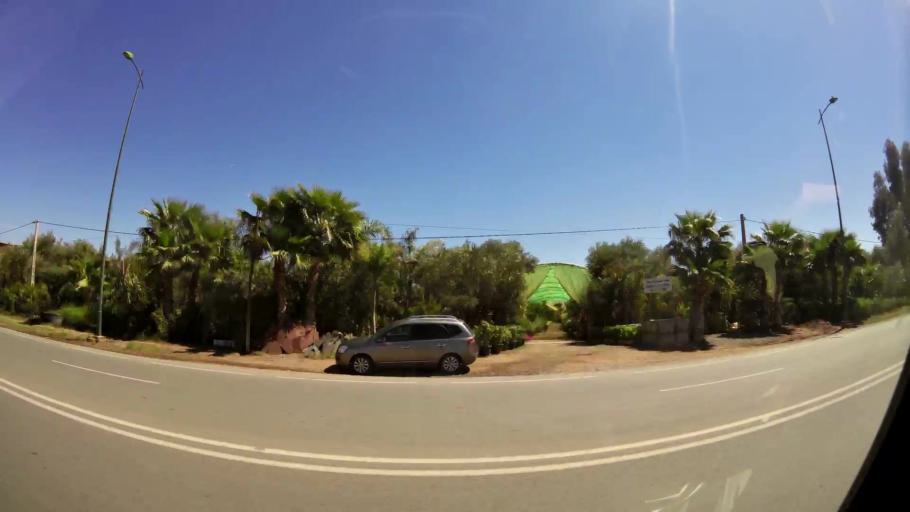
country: MA
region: Marrakech-Tensift-Al Haouz
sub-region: Marrakech
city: Marrakesh
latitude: 31.5659
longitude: -7.9807
